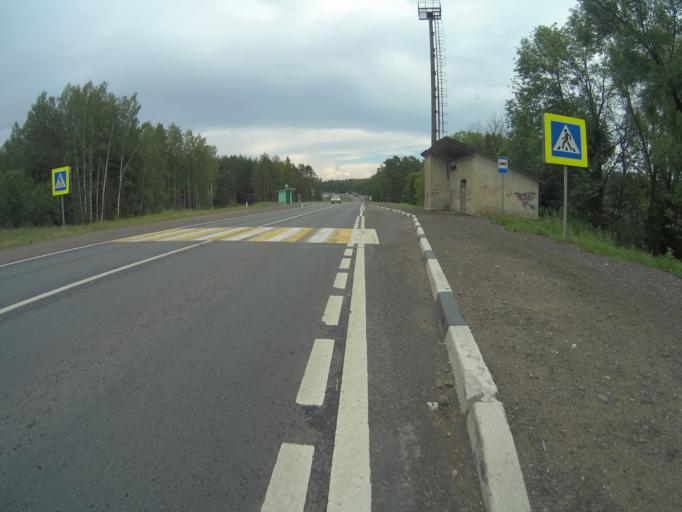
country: RU
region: Vladimir
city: Kameshkovo
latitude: 56.1944
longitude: 40.9212
